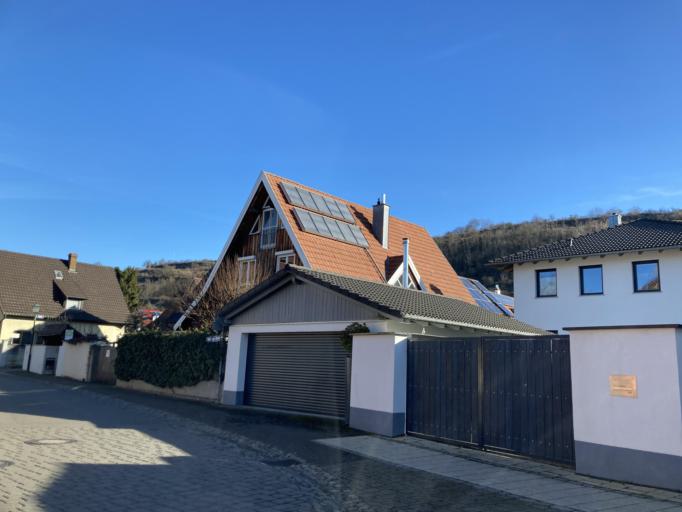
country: DE
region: Baden-Wuerttemberg
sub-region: Freiburg Region
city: Merdingen
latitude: 47.9860
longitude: 7.6712
